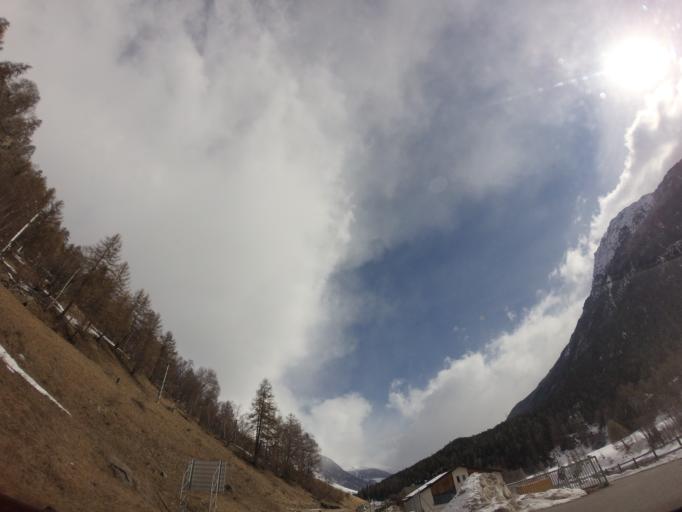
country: CH
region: Grisons
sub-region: Inn District
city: Zernez
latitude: 46.7549
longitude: 10.0829
